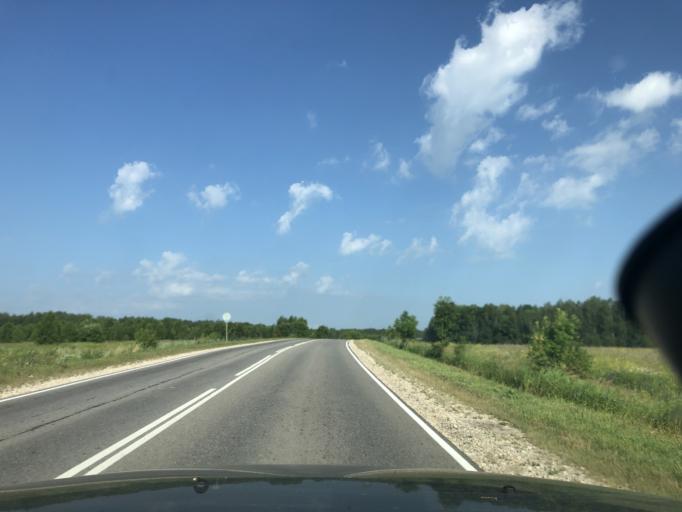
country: RU
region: Tula
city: Dubna
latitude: 54.1326
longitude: 37.0303
